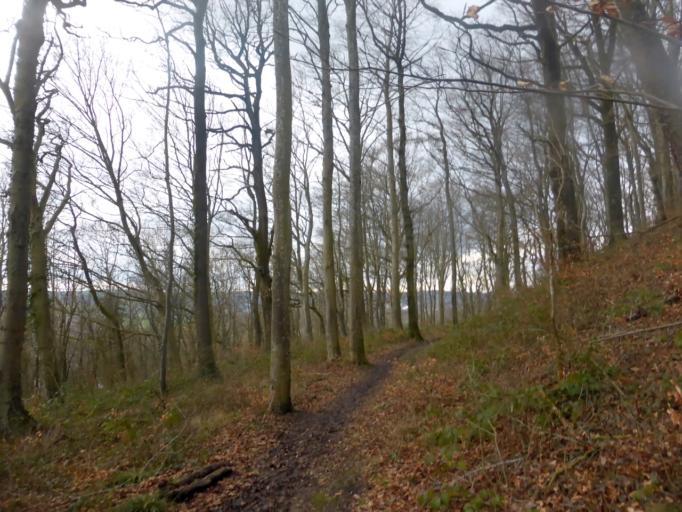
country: LU
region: Luxembourg
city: Belvaux
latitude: 49.5196
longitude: 5.9333
